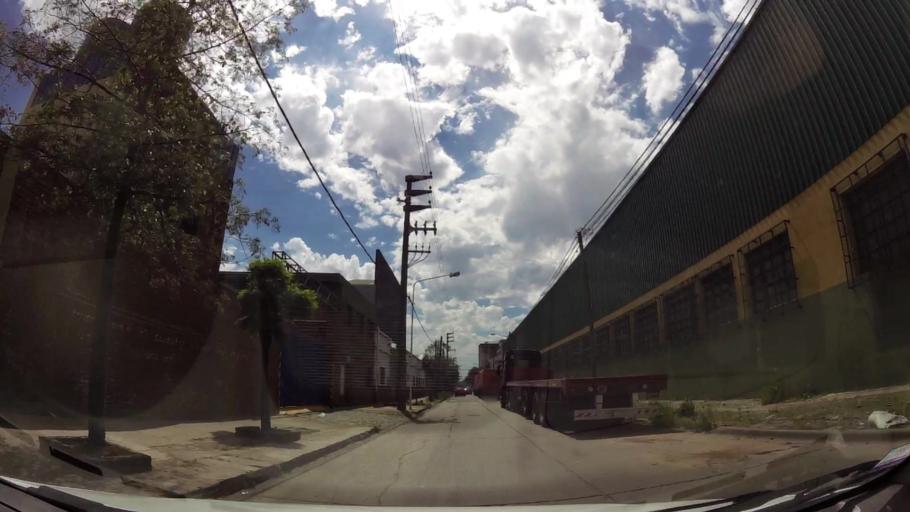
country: AR
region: Buenos Aires
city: San Justo
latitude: -34.6806
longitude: -58.5478
